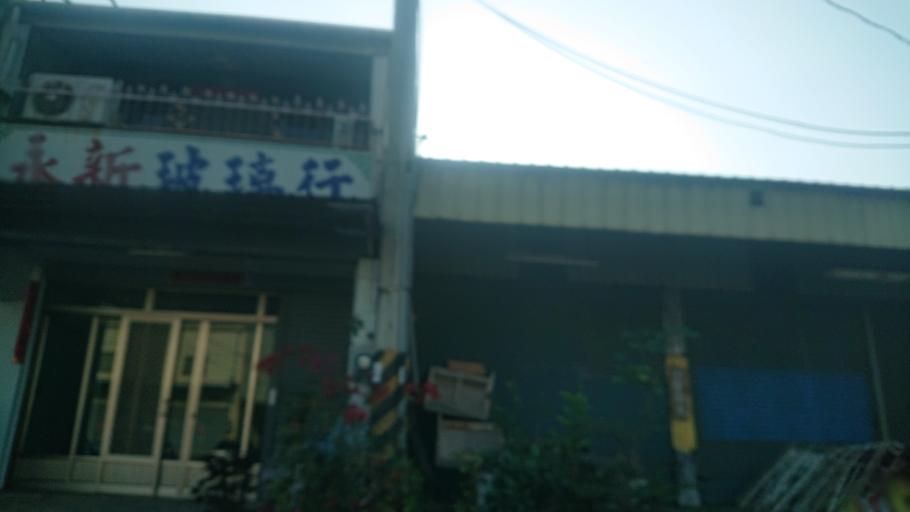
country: TW
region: Taiwan
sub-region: Tainan
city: Tainan
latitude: 23.0721
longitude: 120.2147
